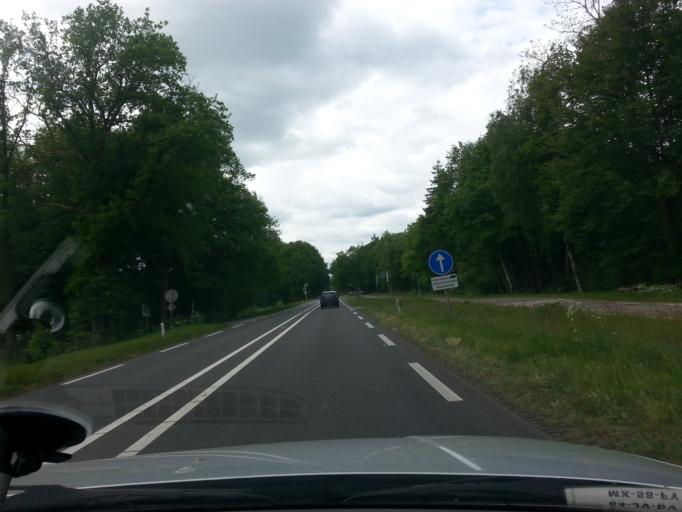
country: NL
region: Overijssel
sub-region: Gemeente Oldenzaal
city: Oldenzaal
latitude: 52.3433
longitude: 6.9665
